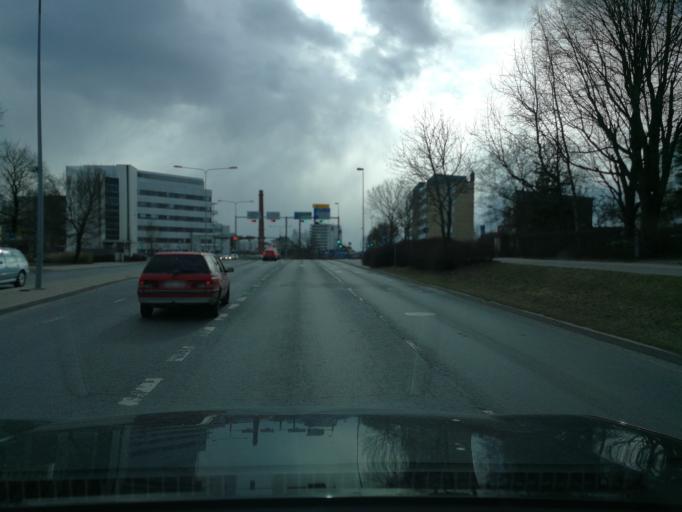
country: FI
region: Varsinais-Suomi
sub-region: Turku
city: Turku
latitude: 60.4560
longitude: 22.2995
